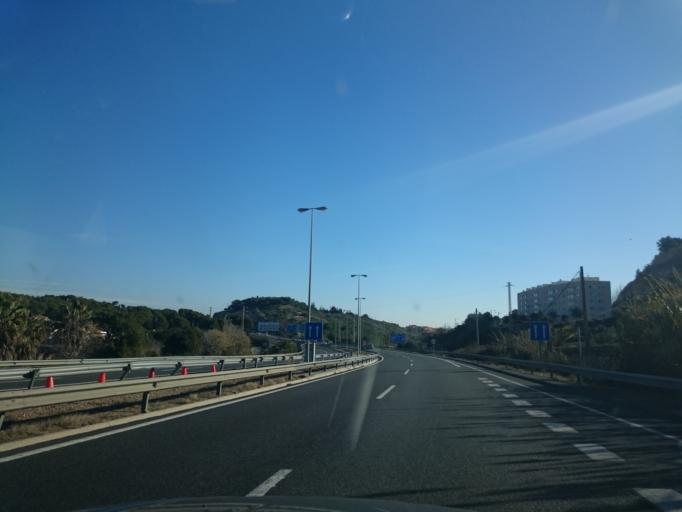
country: ES
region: Catalonia
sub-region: Provincia de Tarragona
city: Tarragona
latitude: 41.1232
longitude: 1.2606
